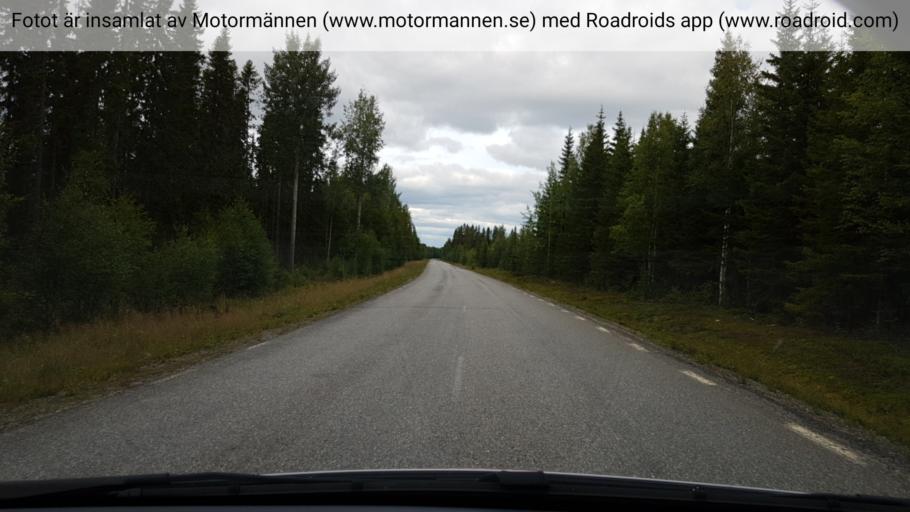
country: SE
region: Vaesterbotten
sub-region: Vannas Kommun
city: Vannasby
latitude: 64.0173
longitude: 19.9303
